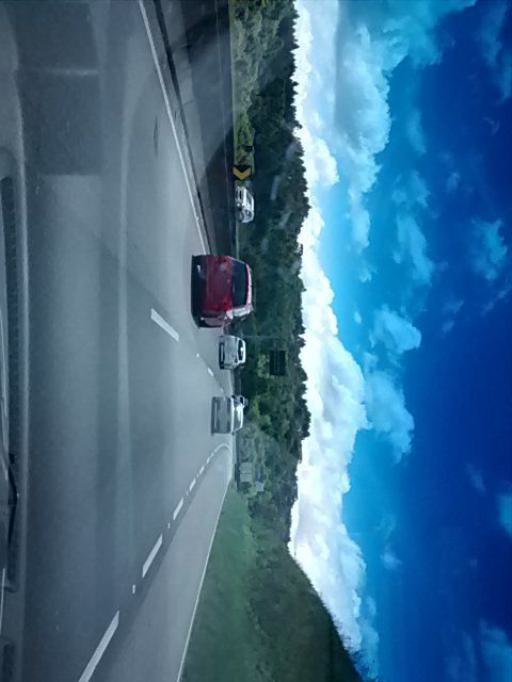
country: BR
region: Parana
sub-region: Campina Grande Do Sul
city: Campina Grande do Sul
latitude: -25.3110
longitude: -49.0144
